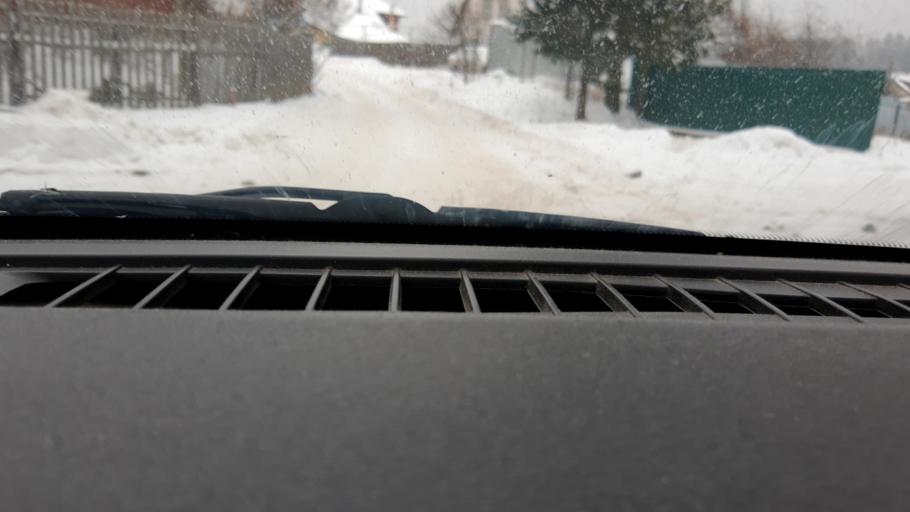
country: RU
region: Nizjnij Novgorod
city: Afonino
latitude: 56.1946
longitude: 44.0613
